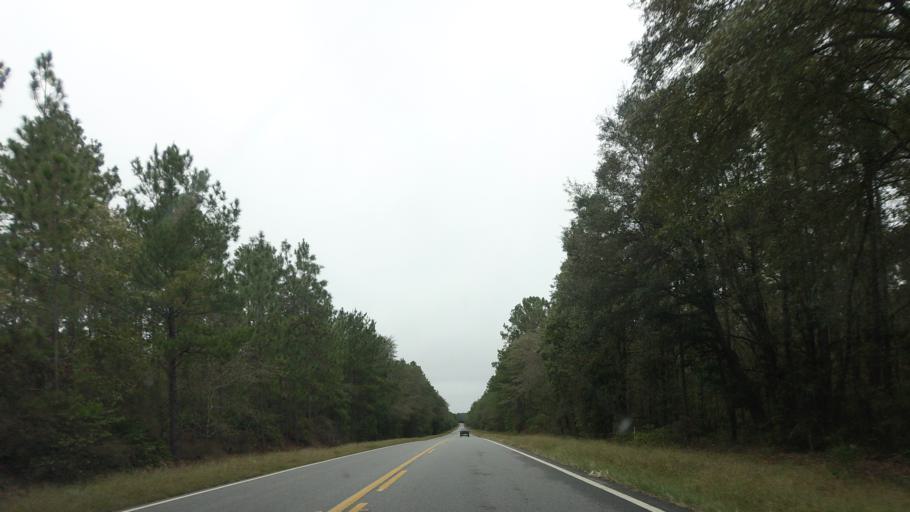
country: US
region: Georgia
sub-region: Berrien County
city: Enigma
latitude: 31.4084
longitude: -83.2418
